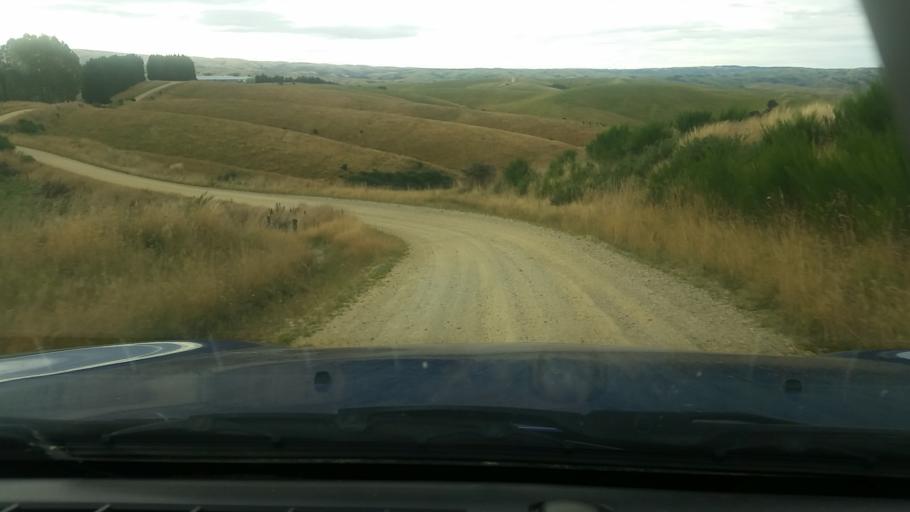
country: NZ
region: Otago
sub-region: Clutha District
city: Balclutha
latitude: -45.7008
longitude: 169.5035
